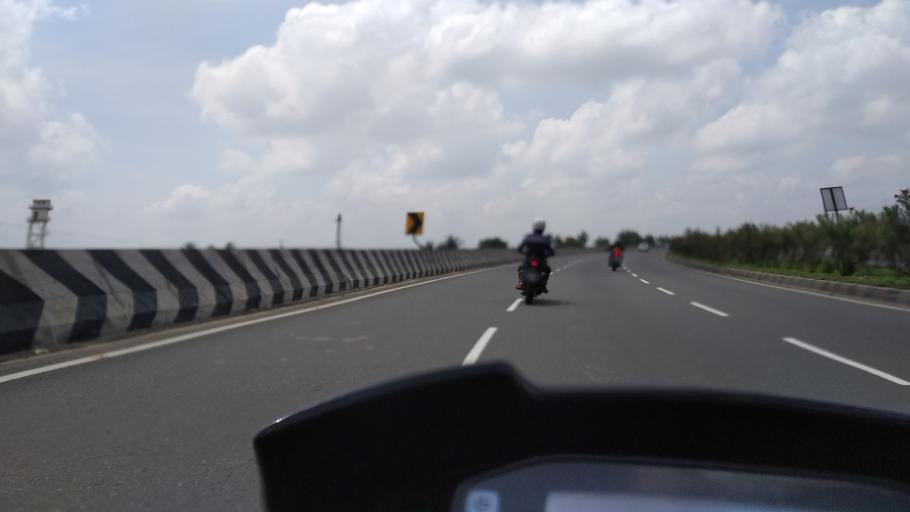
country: IN
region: Tamil Nadu
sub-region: Tiruppur
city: Avinashi
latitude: 11.1286
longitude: 77.1981
